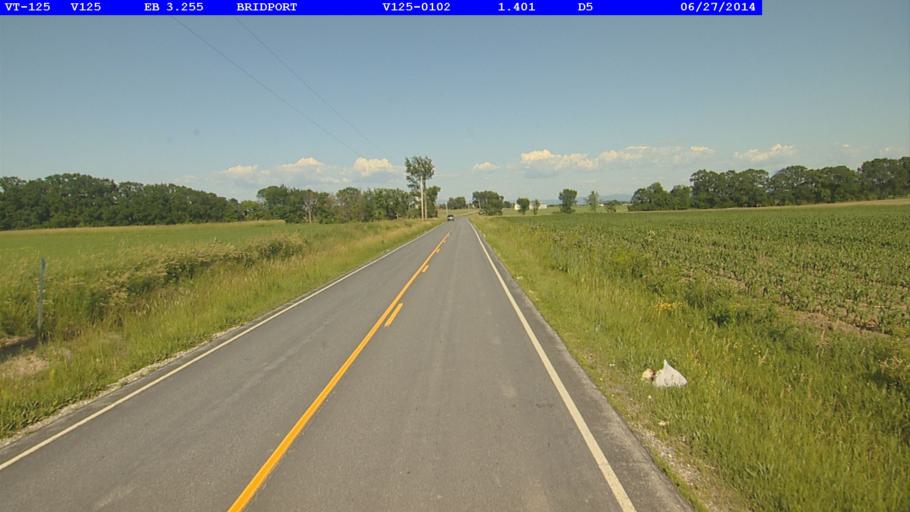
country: US
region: New York
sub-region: Essex County
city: Port Henry
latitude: 44.0047
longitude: -73.3804
